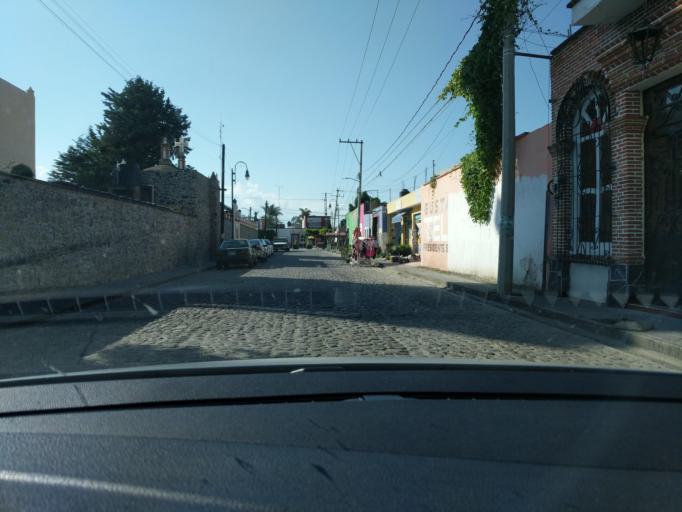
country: MX
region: Puebla
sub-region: San Gregorio Atzompa
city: Chipilo de Francisco Javier Mina
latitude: 19.0299
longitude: -98.3193
